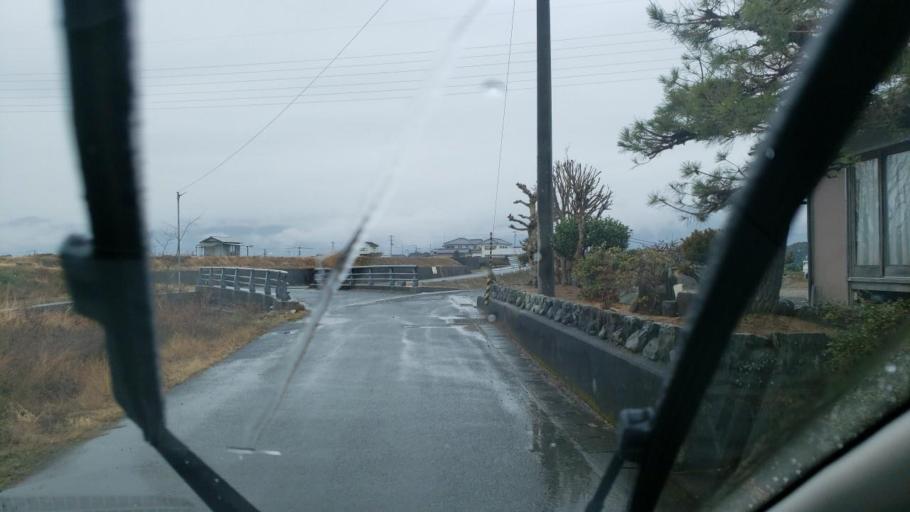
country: JP
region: Tokushima
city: Kamojimacho-jogejima
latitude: 34.0841
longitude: 134.2560
